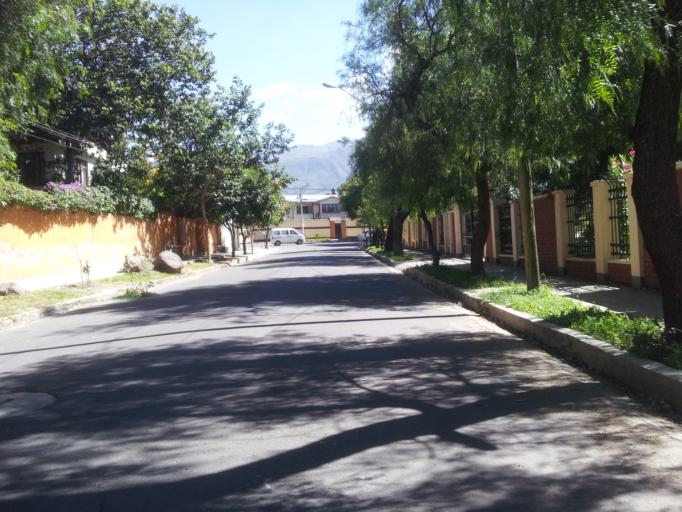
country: BO
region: Cochabamba
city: Cochabamba
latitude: -17.3773
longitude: -66.1744
